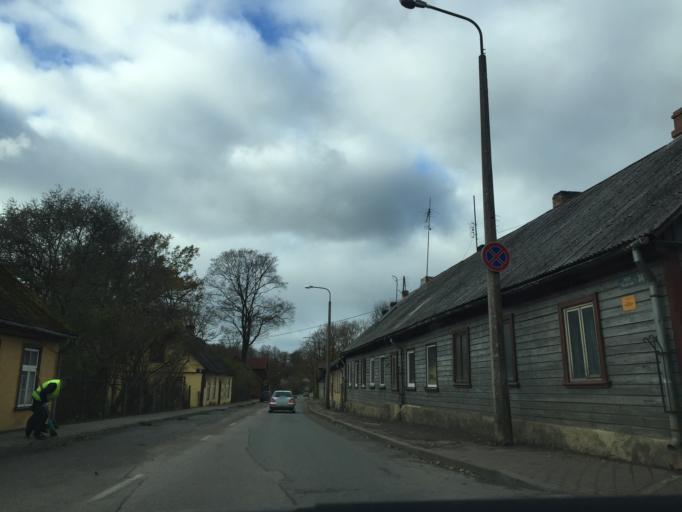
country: LV
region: Tukuma Rajons
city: Tukums
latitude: 56.9674
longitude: 23.1464
